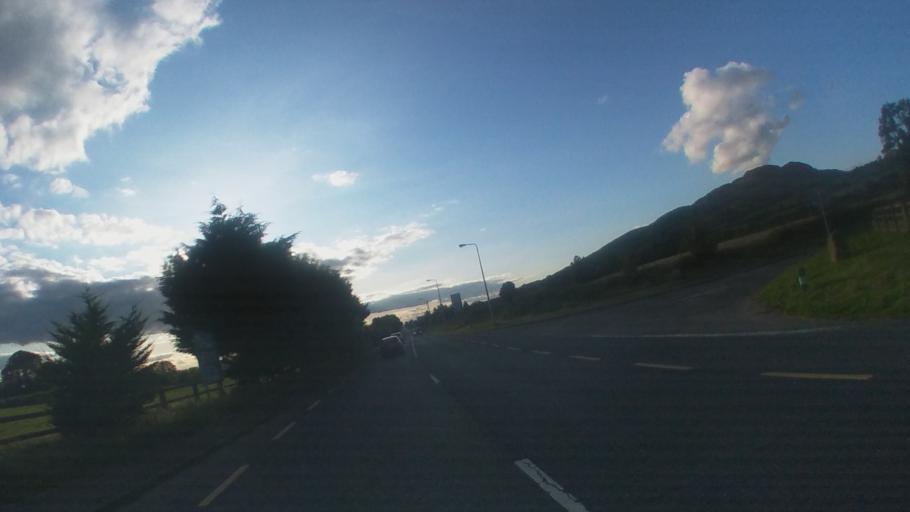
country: IE
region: Leinster
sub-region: Lu
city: Carlingford
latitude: 53.9974
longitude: -6.2453
